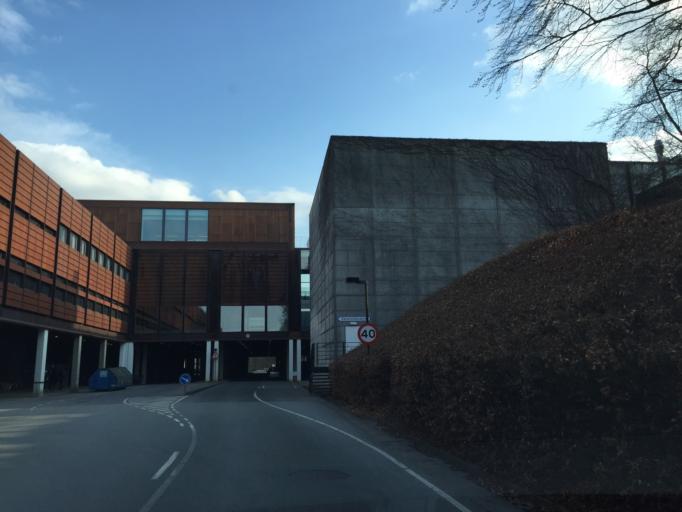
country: DK
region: South Denmark
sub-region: Odense Kommune
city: Neder Holluf
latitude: 55.3686
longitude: 10.4278
